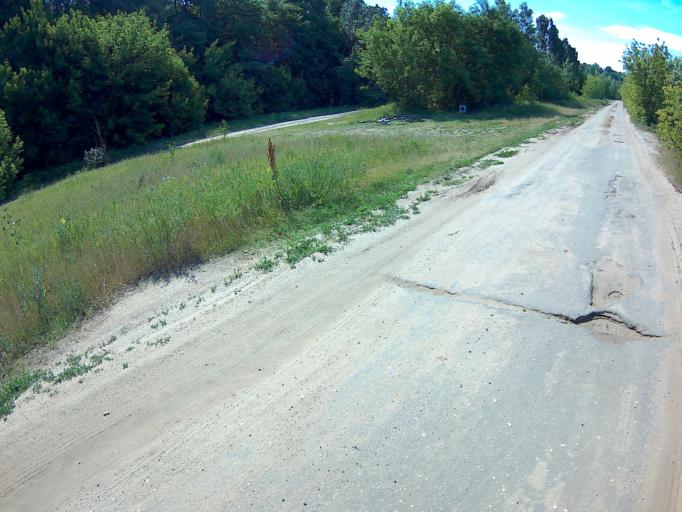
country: RU
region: Nizjnij Novgorod
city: Nizhniy Novgorod
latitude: 56.2587
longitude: 43.9659
